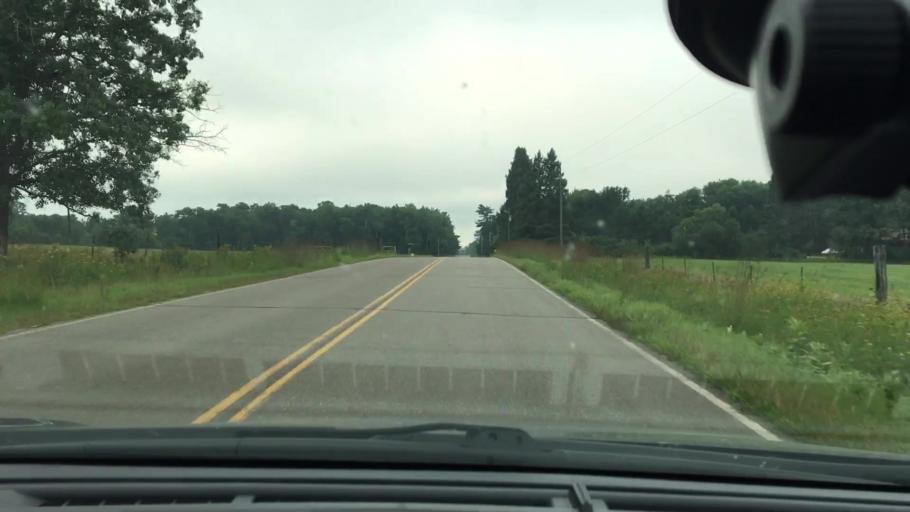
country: US
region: Minnesota
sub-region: Crow Wing County
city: Cross Lake
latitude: 46.6455
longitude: -94.0096
